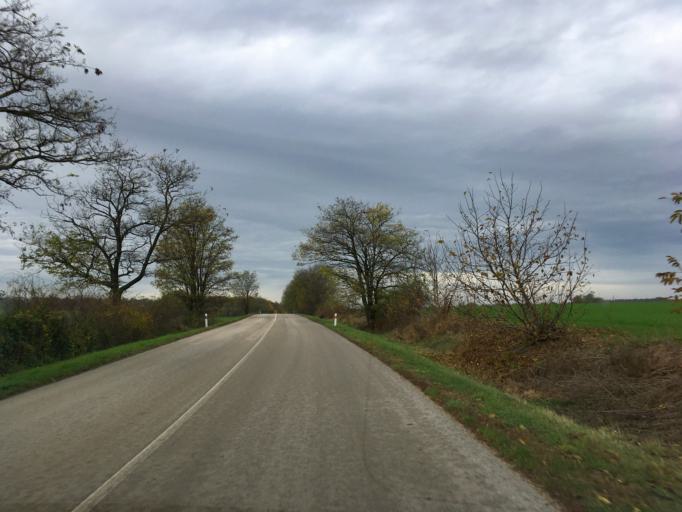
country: SK
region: Nitriansky
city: Svodin
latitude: 48.0290
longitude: 18.3979
